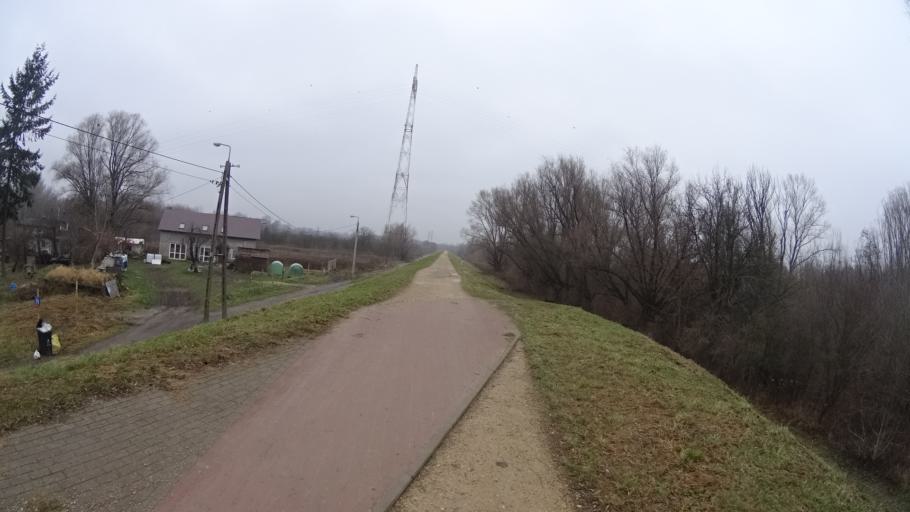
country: PL
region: Masovian Voivodeship
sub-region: Warszawa
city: Wilanow
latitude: 52.1965
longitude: 21.1002
